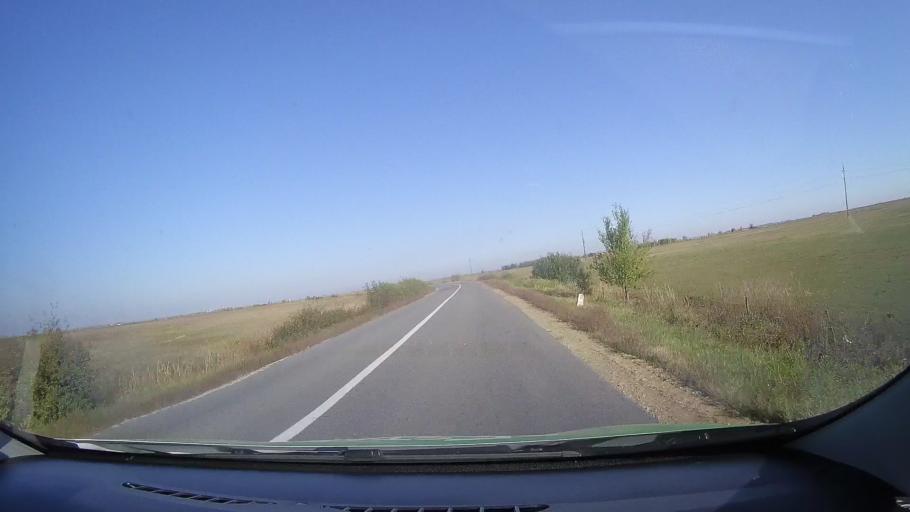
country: RO
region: Satu Mare
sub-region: Comuna Cauas
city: Cauas
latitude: 47.5405
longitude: 22.5639
